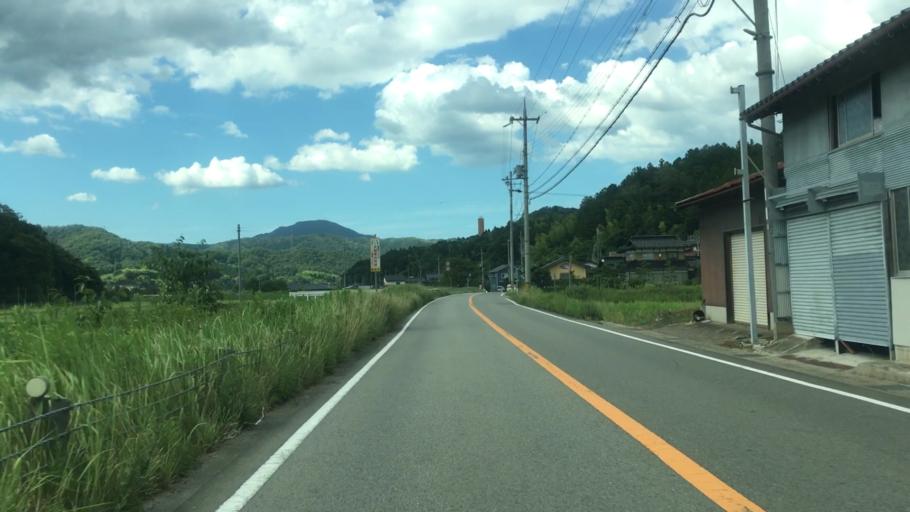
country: JP
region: Hyogo
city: Toyooka
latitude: 35.5384
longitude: 134.7899
